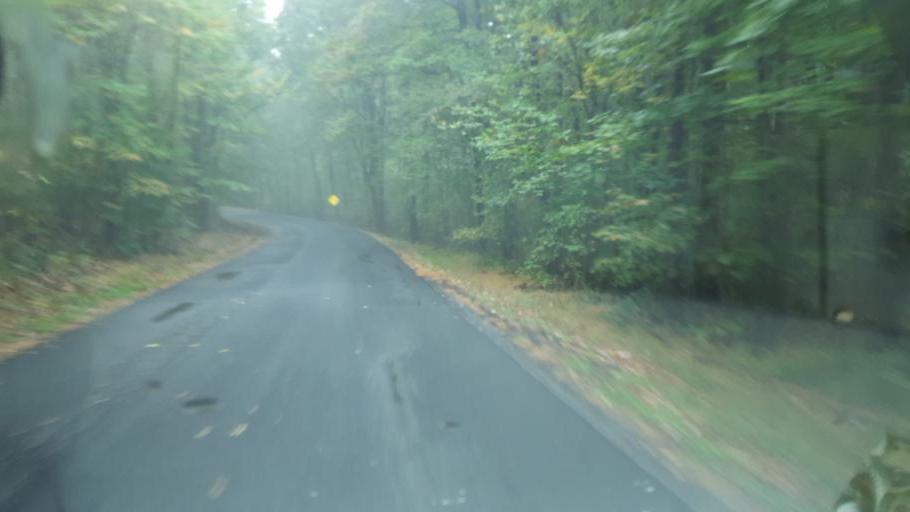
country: US
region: Ohio
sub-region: Ashland County
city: Loudonville
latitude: 40.6027
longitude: -82.3116
